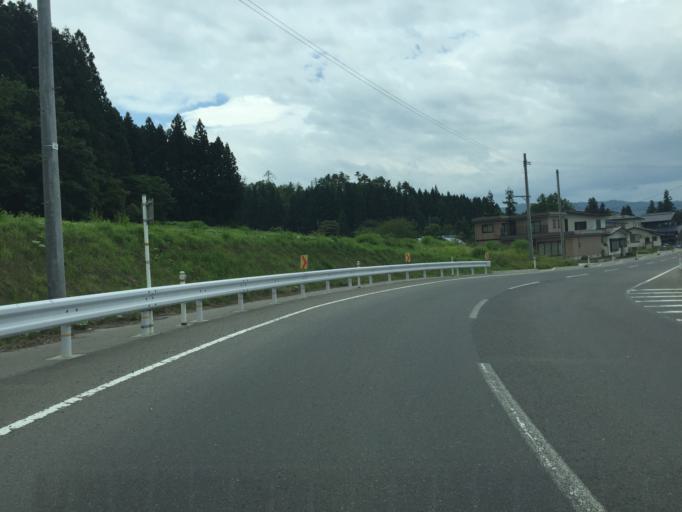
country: JP
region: Yamagata
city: Yonezawa
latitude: 37.8950
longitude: 140.1515
